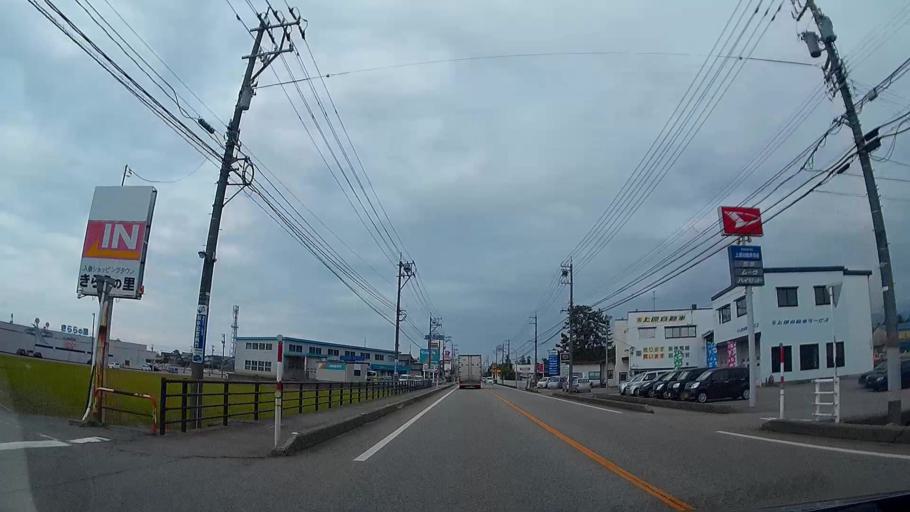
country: JP
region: Toyama
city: Nyuzen
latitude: 36.9288
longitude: 137.4975
